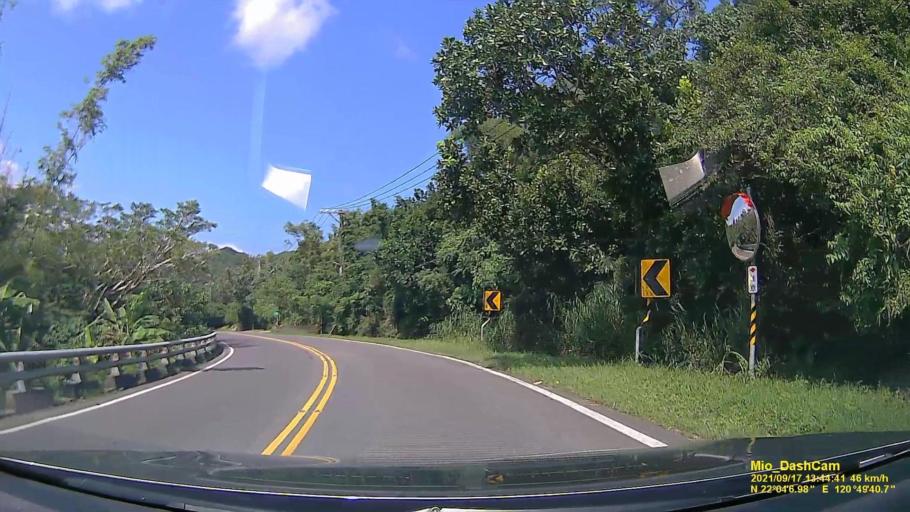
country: TW
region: Taiwan
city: Hengchun
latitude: 22.0687
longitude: 120.8281
